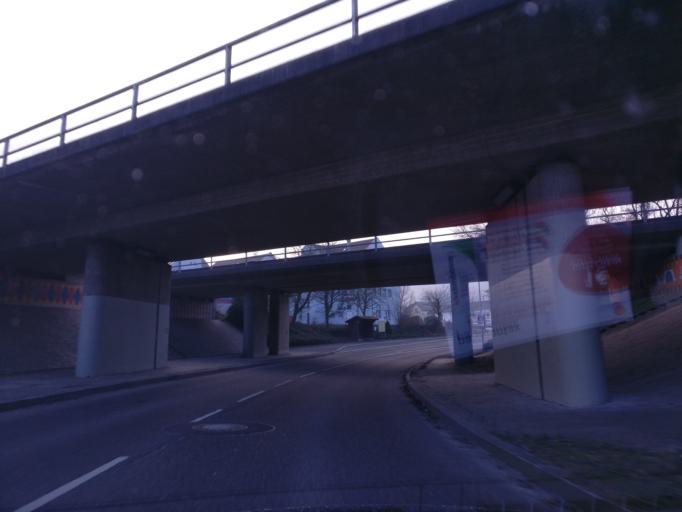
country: DE
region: Baden-Wuerttemberg
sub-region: Regierungsbezirk Stuttgart
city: Lorch
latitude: 48.7992
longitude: 9.6834
